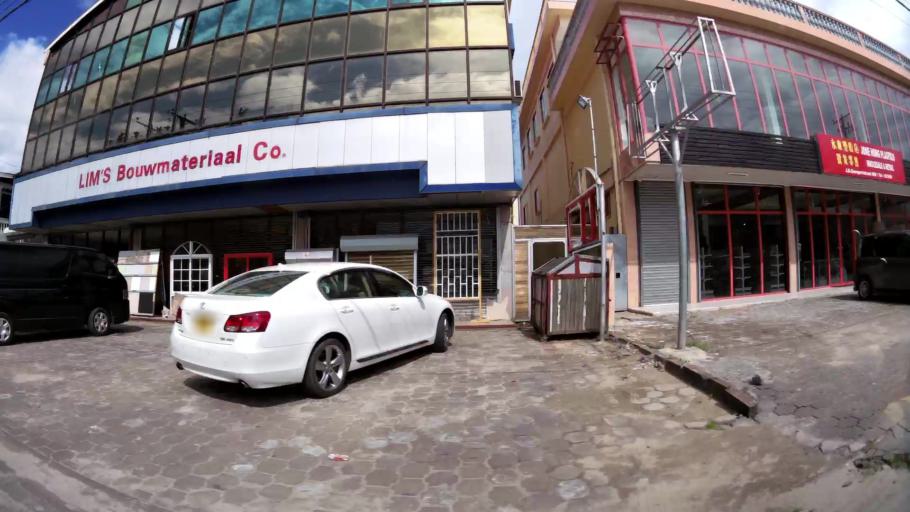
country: SR
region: Paramaribo
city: Paramaribo
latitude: 5.8462
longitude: -55.1415
